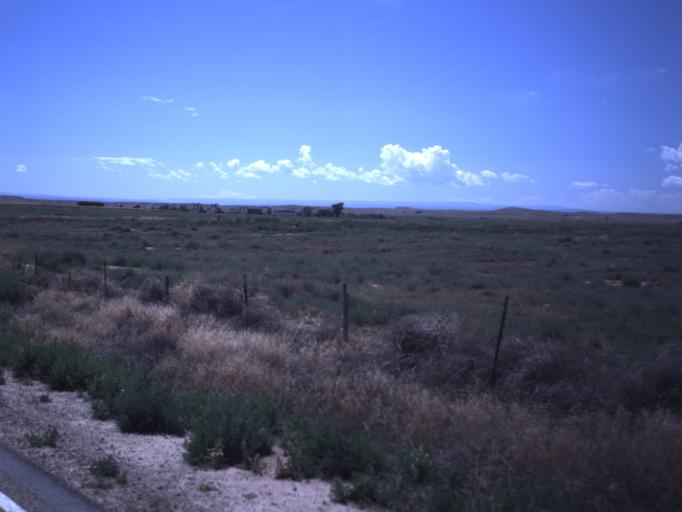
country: US
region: Utah
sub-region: Uintah County
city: Naples
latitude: 40.1731
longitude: -109.6645
